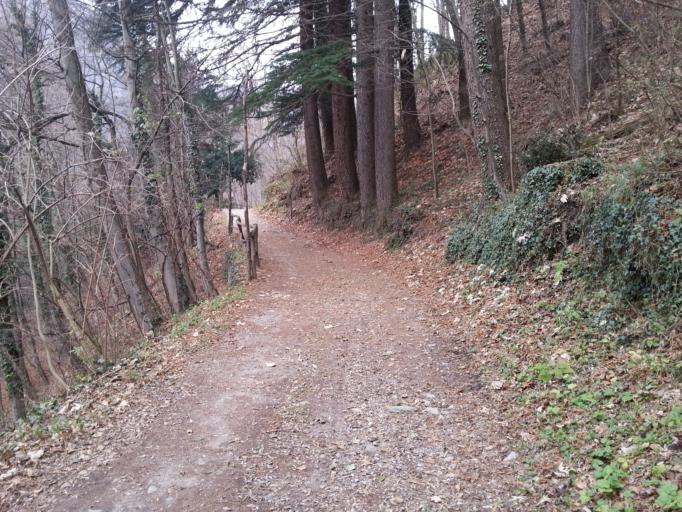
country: CH
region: Ticino
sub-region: Mendrisio District
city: Morbio Inferiore
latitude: 45.8650
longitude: 9.0271
